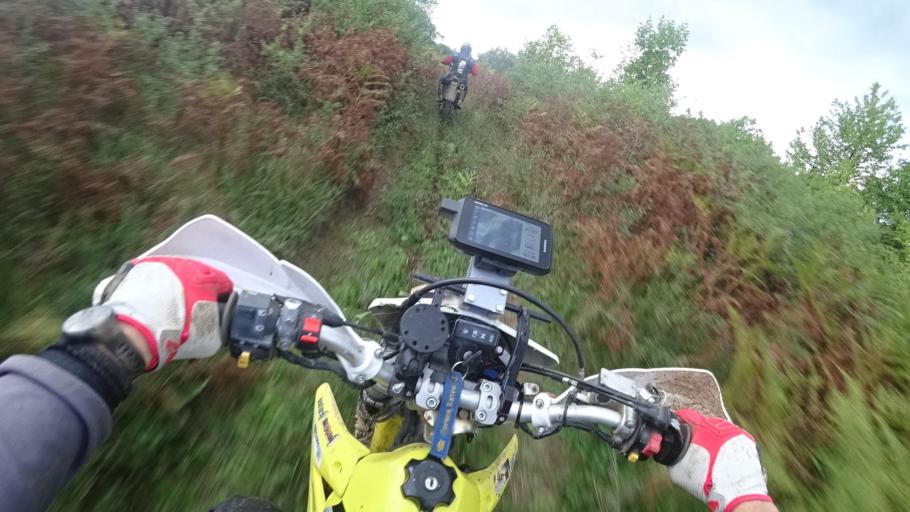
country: BA
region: Republika Srpska
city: Starcevica
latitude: 44.7066
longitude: 17.2203
